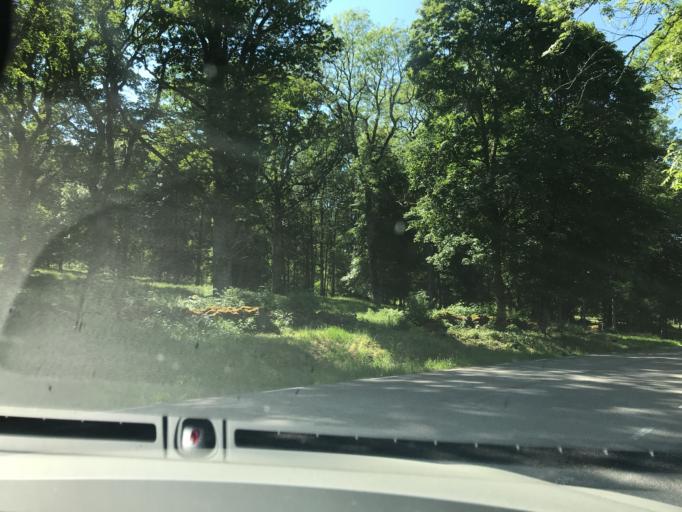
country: SE
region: Vaestra Goetaland
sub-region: Gotene Kommun
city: Goetene
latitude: 58.6216
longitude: 13.4223
